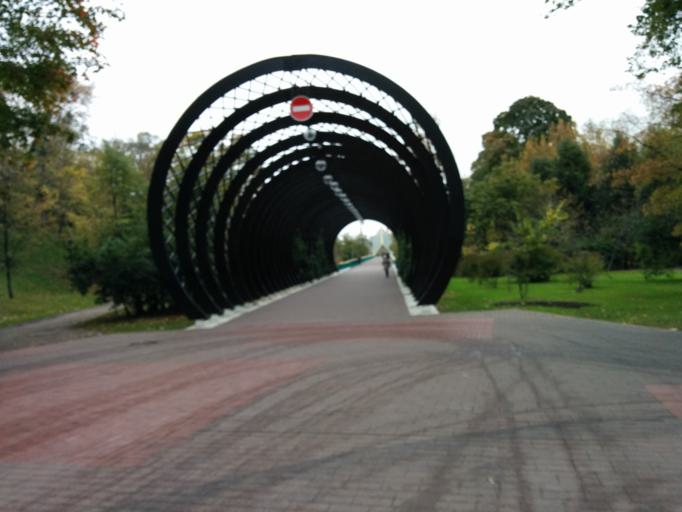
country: RU
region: Moscow
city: Novyye Cheremushki
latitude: 55.7225
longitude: 37.5975
